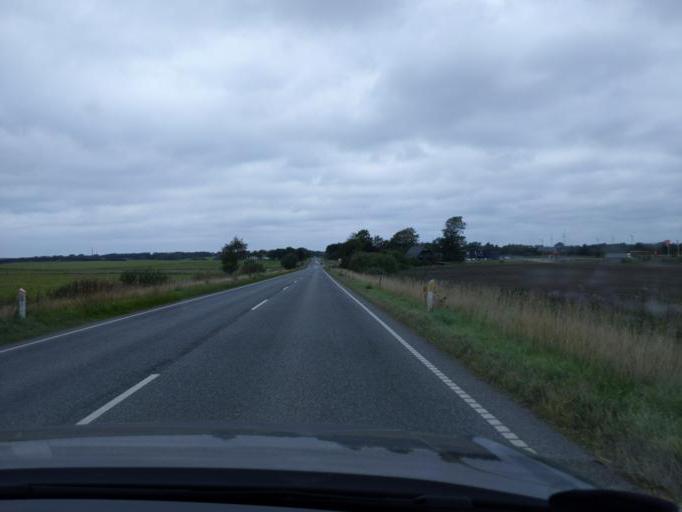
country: DK
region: North Denmark
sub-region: Mariagerfjord Kommune
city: Mariager
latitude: 56.5374
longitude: 9.9003
